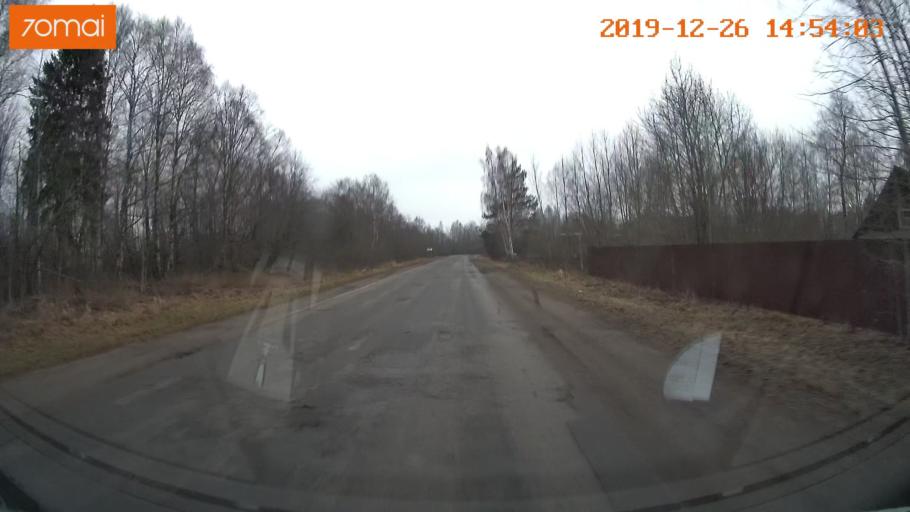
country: RU
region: Jaroslavl
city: Rybinsk
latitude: 58.3103
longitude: 38.8863
